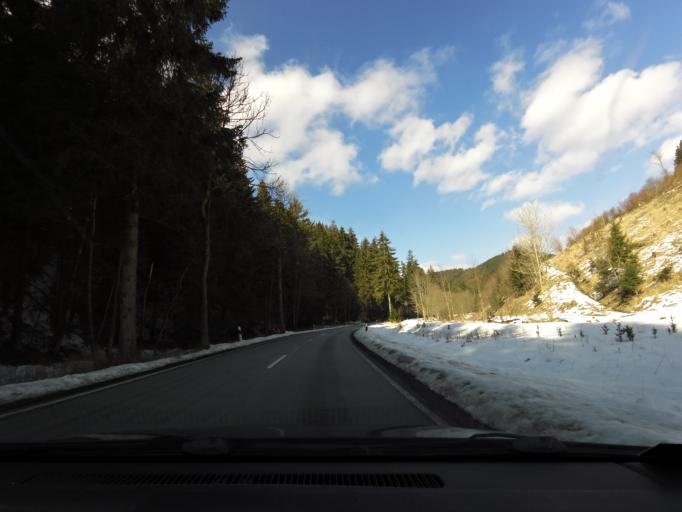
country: DE
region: Lower Saxony
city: Sankt Andreasberg
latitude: 51.6830
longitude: 10.4982
